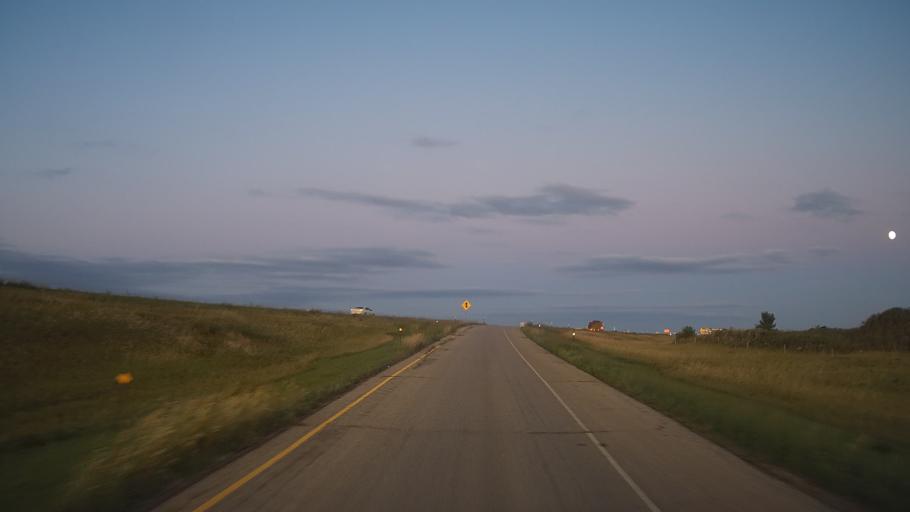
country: US
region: South Dakota
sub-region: Lyman County
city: Kennebec
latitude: 43.8633
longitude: -99.6051
